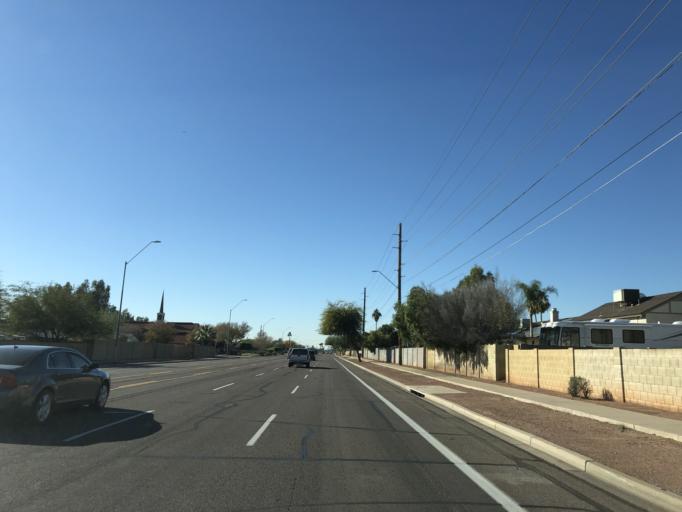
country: US
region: Arizona
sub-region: Maricopa County
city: Peoria
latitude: 33.6546
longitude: -112.1632
